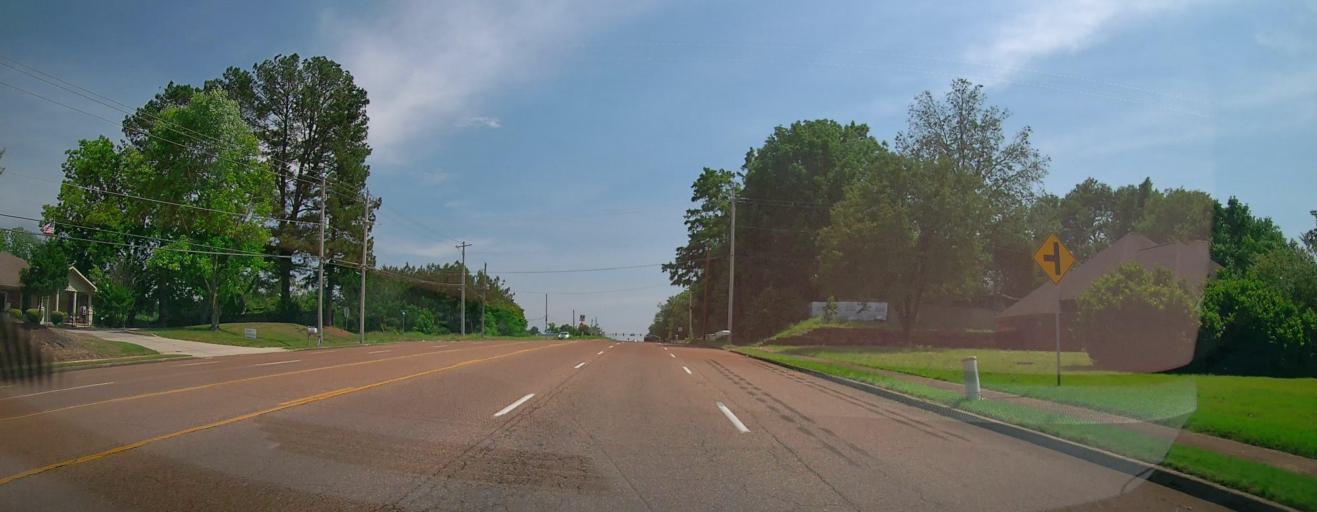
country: US
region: Mississippi
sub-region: De Soto County
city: Olive Branch
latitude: 34.9982
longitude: -89.8309
